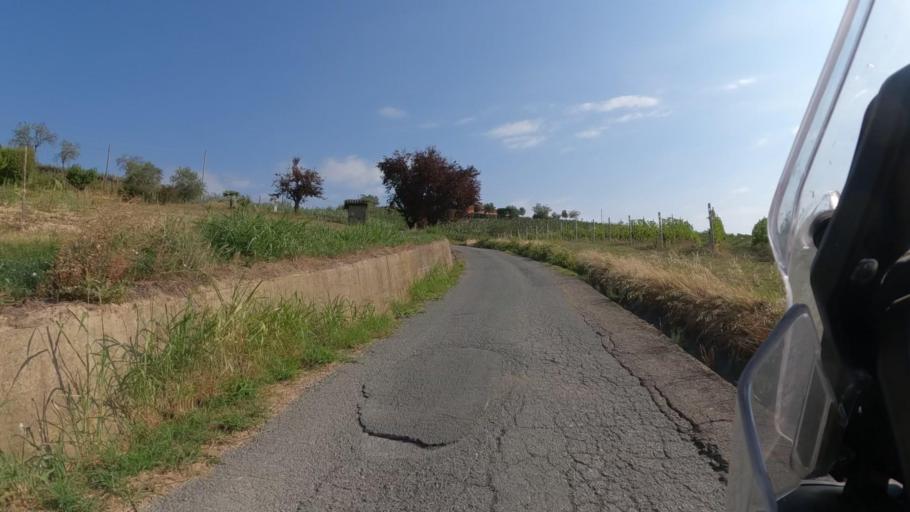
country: IT
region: Piedmont
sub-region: Provincia di Asti
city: Castel Boglione
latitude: 44.7455
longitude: 8.3871
